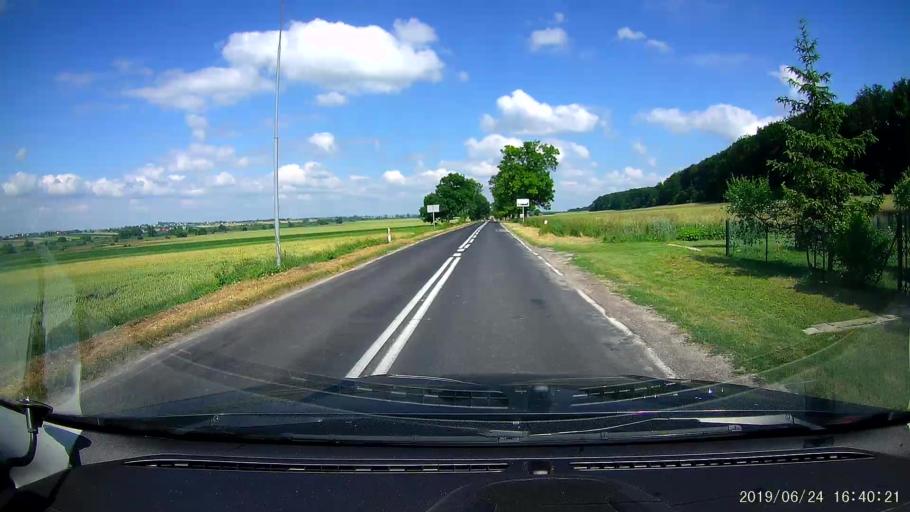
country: PL
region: Lublin Voivodeship
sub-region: Powiat tomaszowski
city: Rachanie
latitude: 50.5302
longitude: 23.5698
